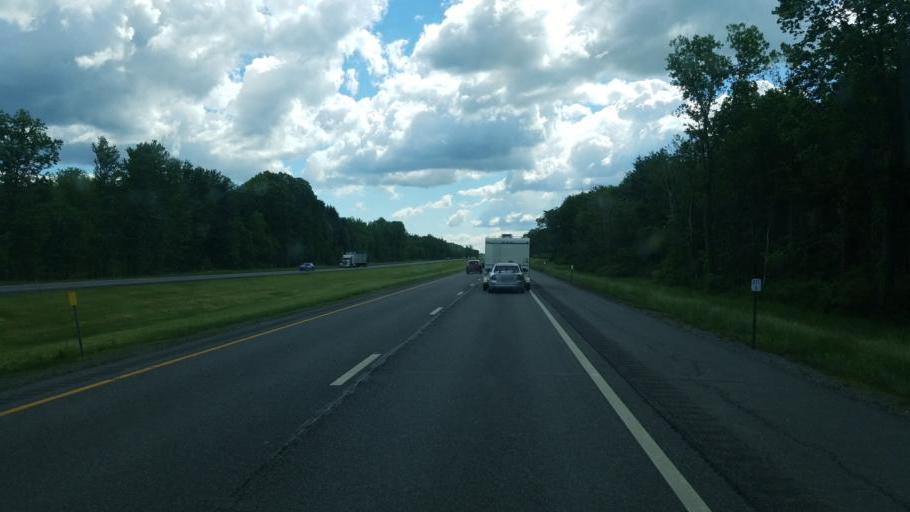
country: US
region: New York
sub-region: Onondaga County
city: Minoa
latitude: 43.0917
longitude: -75.9452
